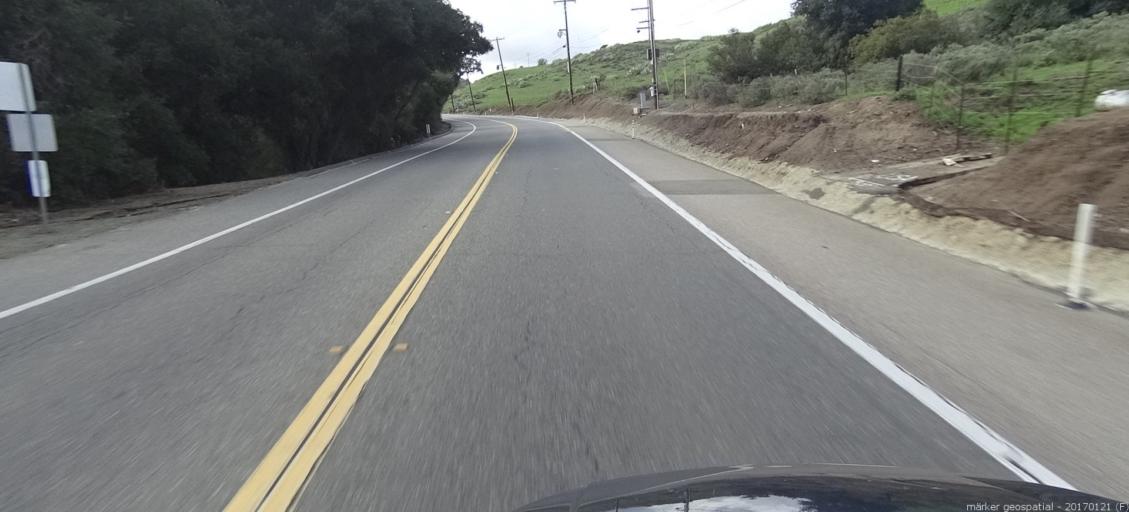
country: US
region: California
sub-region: Orange County
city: Portola Hills
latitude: 33.6917
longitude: -117.6272
